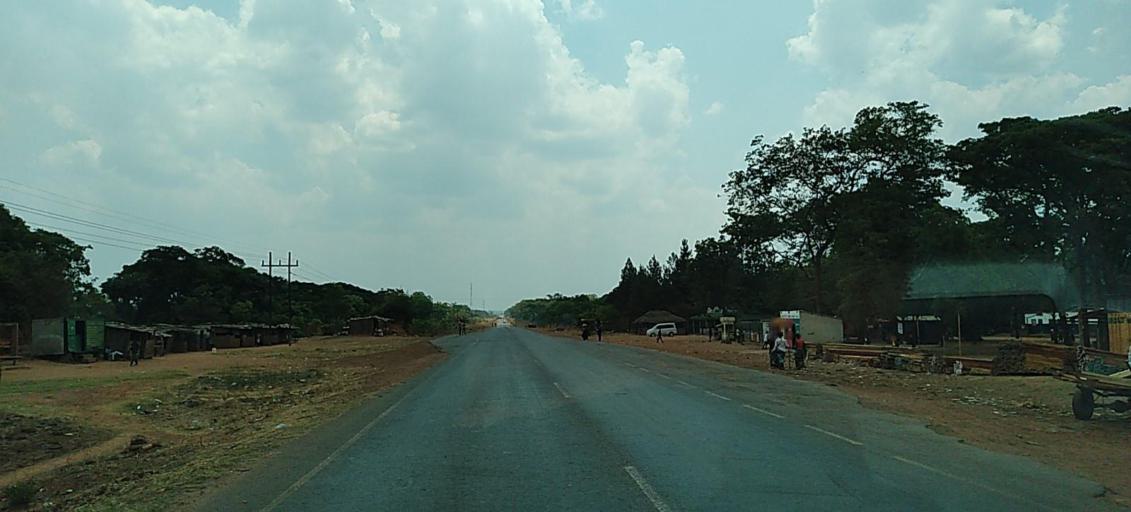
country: ZM
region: Copperbelt
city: Kalulushi
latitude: -12.8423
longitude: 28.0052
